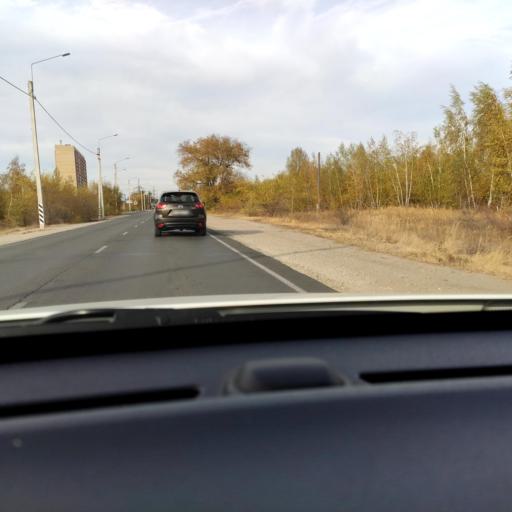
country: RU
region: Voronezj
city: Maslovka
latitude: 51.5855
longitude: 39.2479
